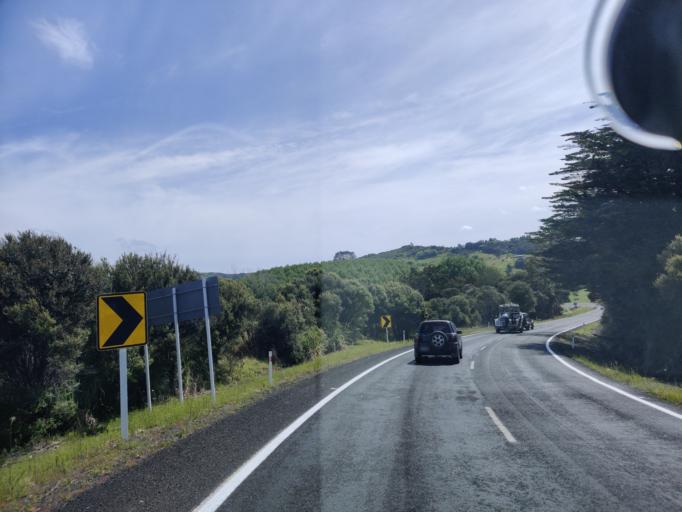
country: NZ
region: Northland
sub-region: Far North District
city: Kaitaia
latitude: -35.4596
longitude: 173.4688
